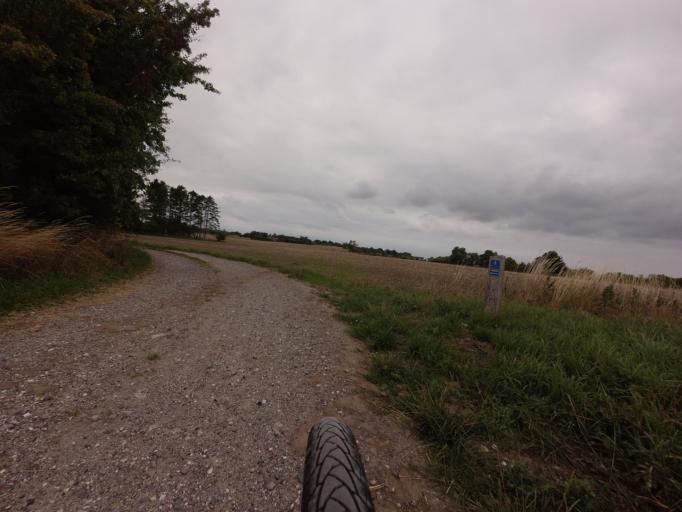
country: DK
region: Zealand
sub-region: Stevns Kommune
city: Store Heddinge
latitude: 55.3312
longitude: 12.4491
